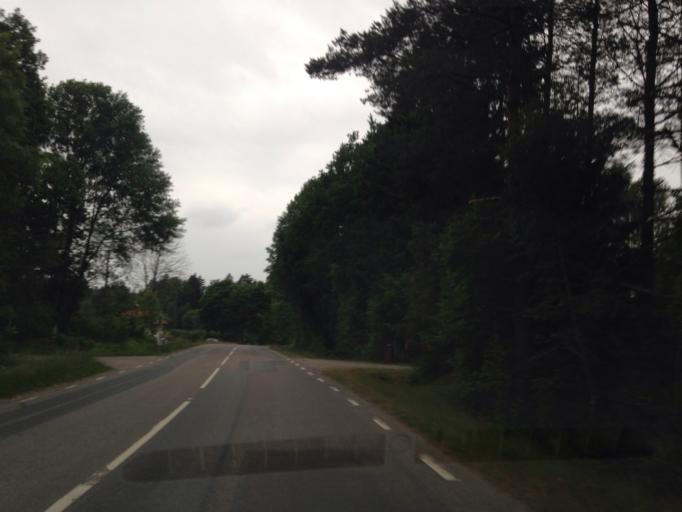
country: SE
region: Vaestra Goetaland
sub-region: Harryda Kommun
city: Hindas
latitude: 57.6756
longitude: 12.3364
